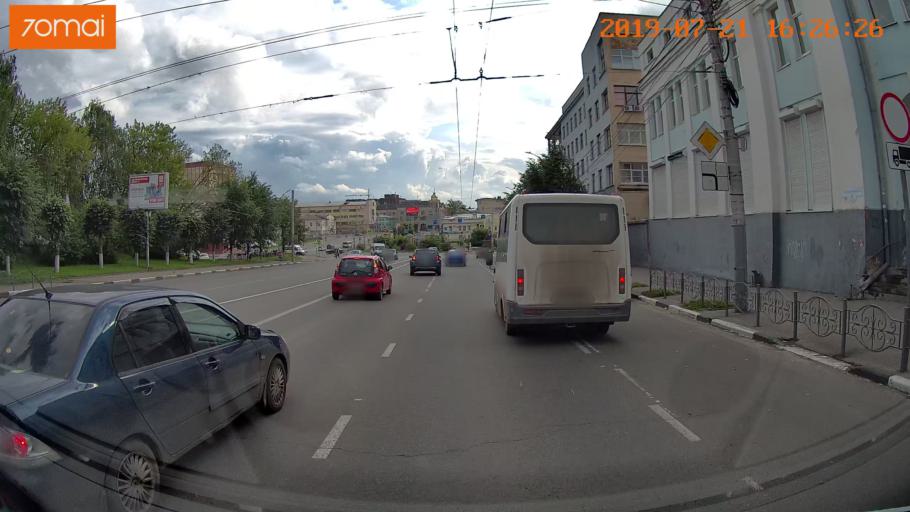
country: RU
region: Ivanovo
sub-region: Gorod Ivanovo
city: Ivanovo
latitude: 56.9976
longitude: 40.9818
